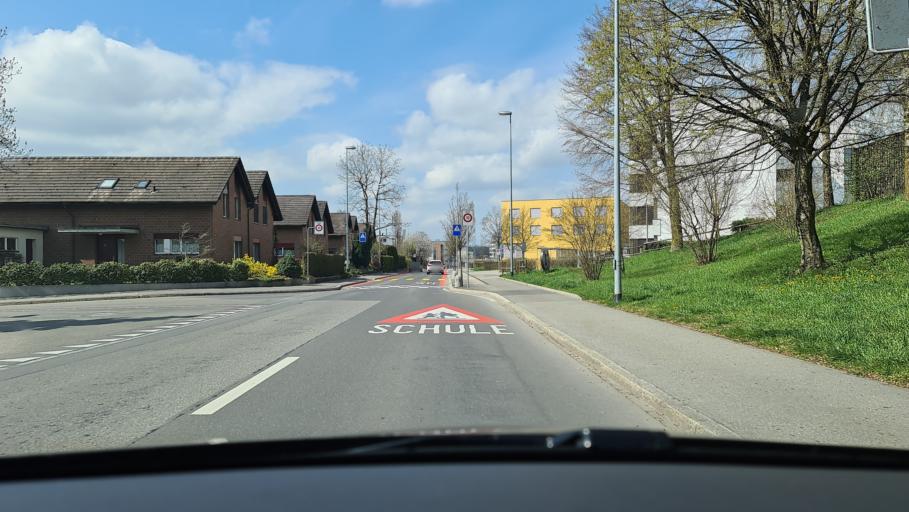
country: CH
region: Zug
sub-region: Zug
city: Steinhausen
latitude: 47.1973
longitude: 8.4908
